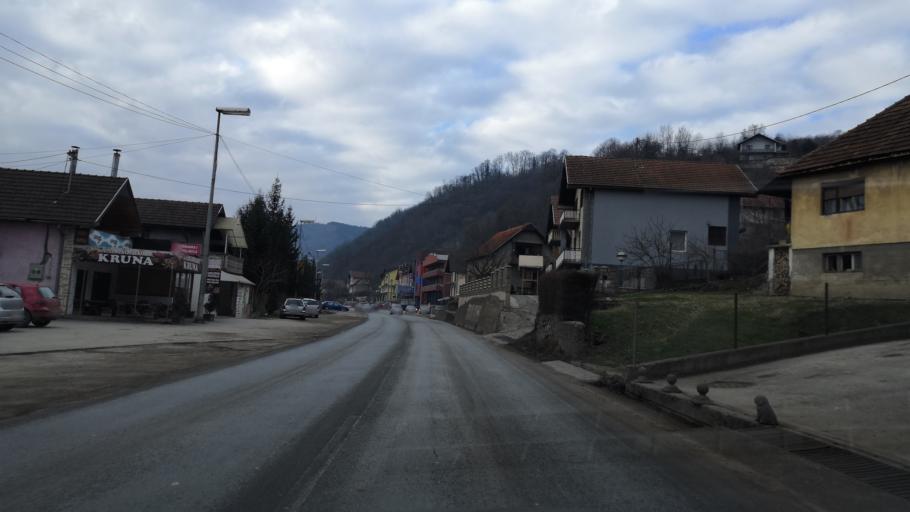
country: BA
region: Republika Srpska
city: Zvornik
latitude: 44.4058
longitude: 19.1202
